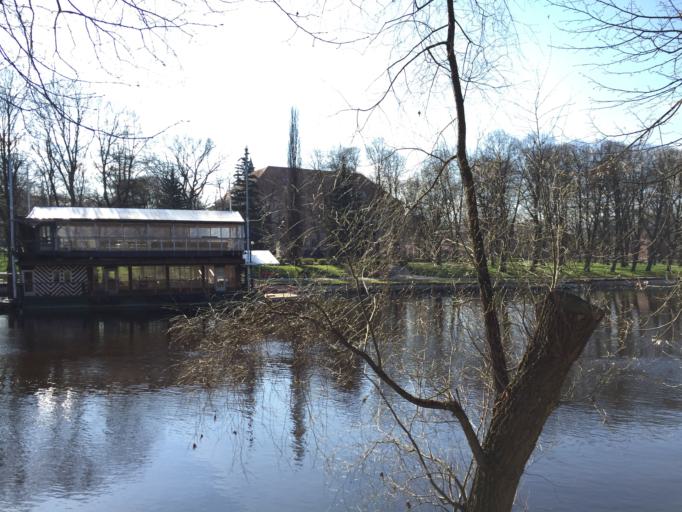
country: EE
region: Tartu
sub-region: Tartu linn
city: Tartu
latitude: 58.3825
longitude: 26.7263
